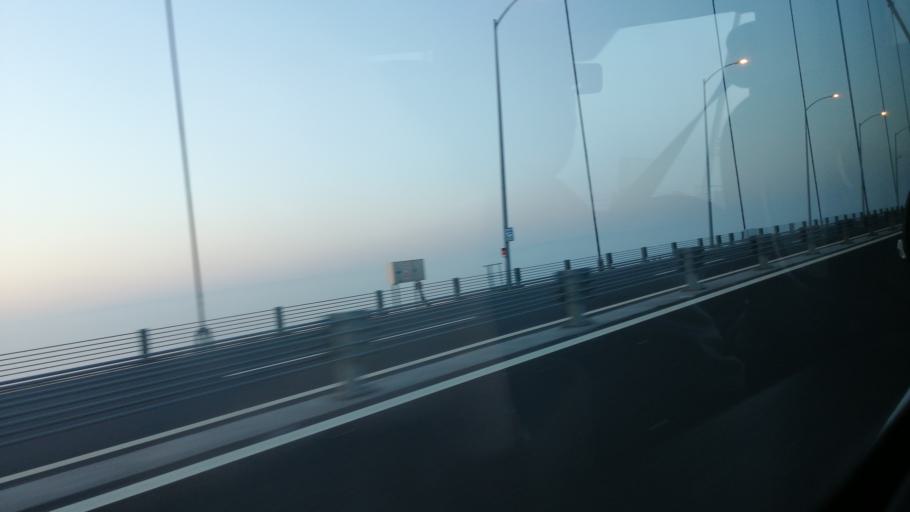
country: TR
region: Yalova
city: Altinova
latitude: 40.7502
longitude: 29.5151
